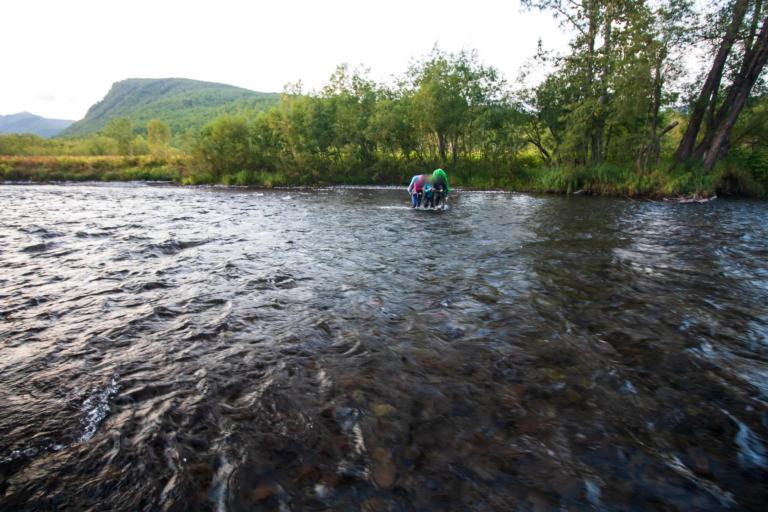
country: RU
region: Kamtsjatka
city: Yelizovo
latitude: 53.8176
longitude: 158.4823
